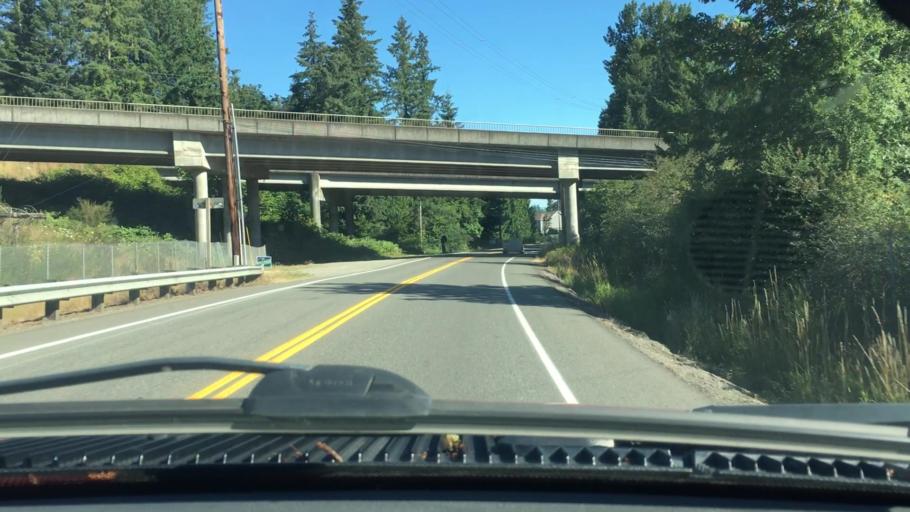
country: US
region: Washington
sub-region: King County
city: Covington
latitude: 47.3473
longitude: -122.1385
